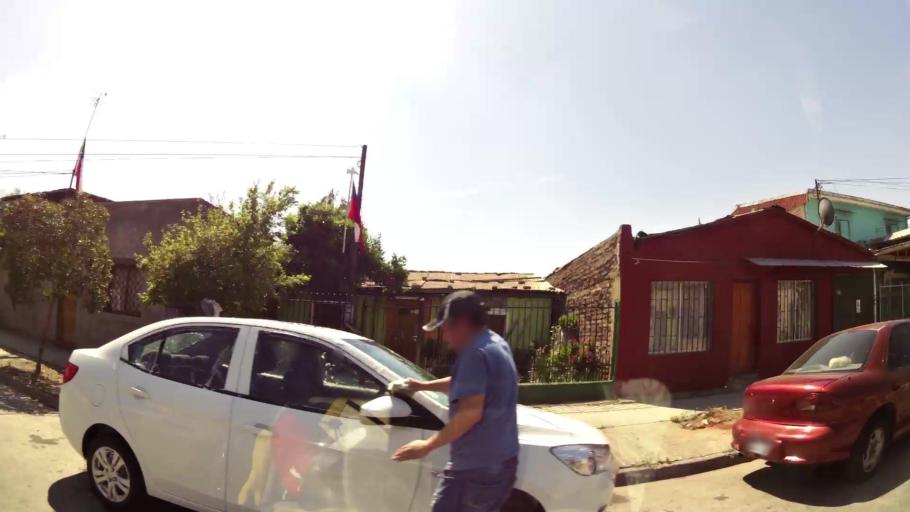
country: CL
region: Santiago Metropolitan
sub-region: Provincia de Santiago
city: La Pintana
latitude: -33.5310
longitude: -70.6455
